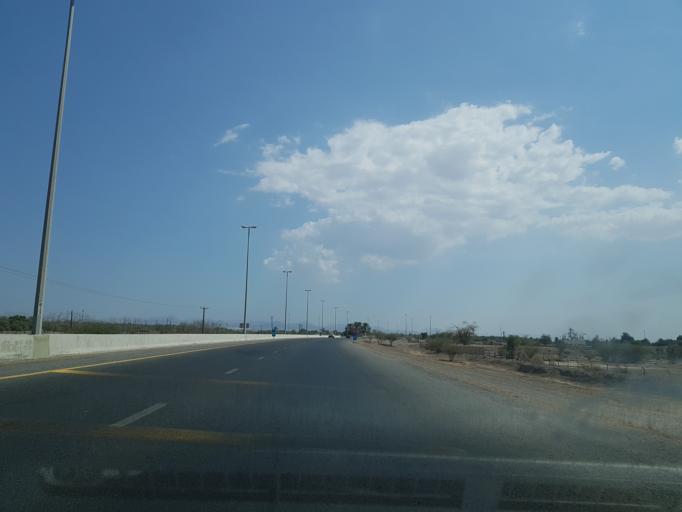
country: AE
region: Ash Shariqah
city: Adh Dhayd
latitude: 25.2453
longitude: 55.9117
